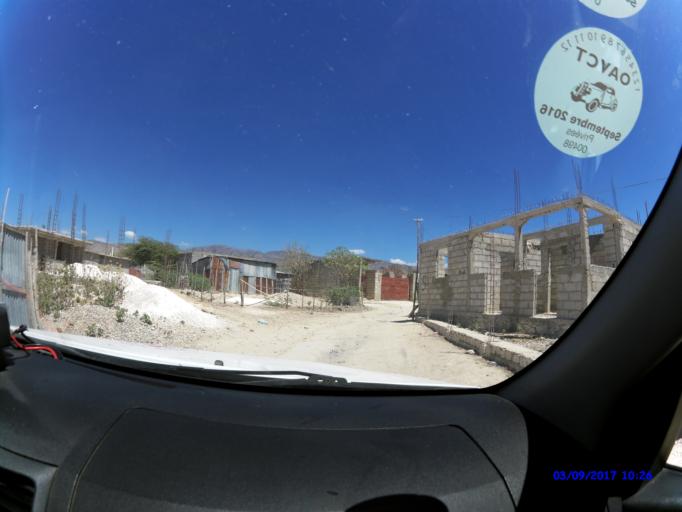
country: HT
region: Ouest
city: Croix des Bouquets
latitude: 18.6477
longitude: -72.2689
